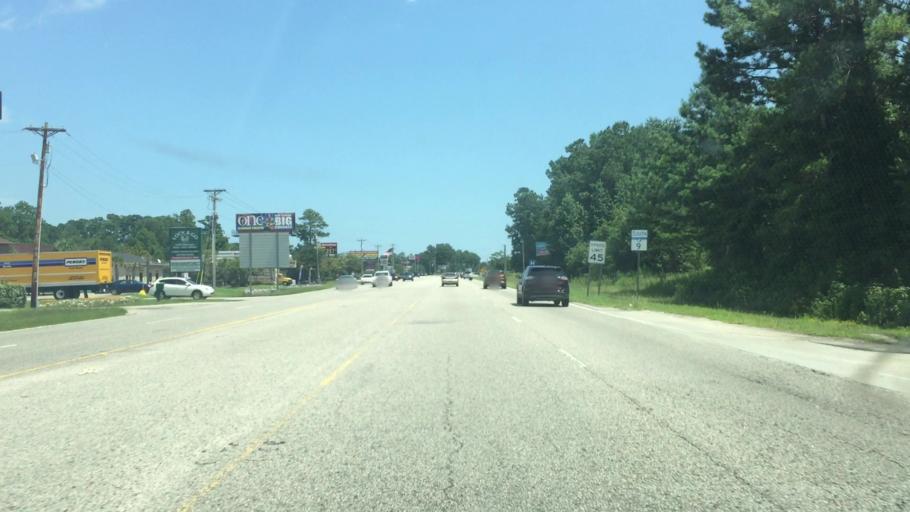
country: US
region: South Carolina
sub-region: Horry County
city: North Myrtle Beach
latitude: 33.8741
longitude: -78.6783
